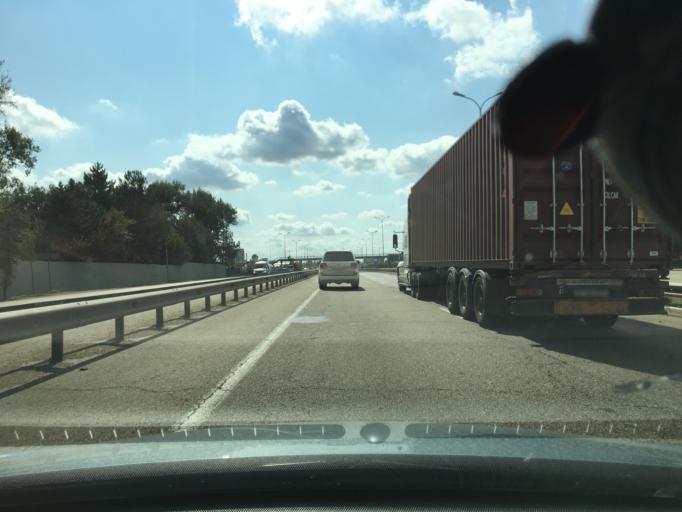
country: RU
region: Krasnodarskiy
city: Kushchevskaya
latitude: 46.5738
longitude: 39.6721
